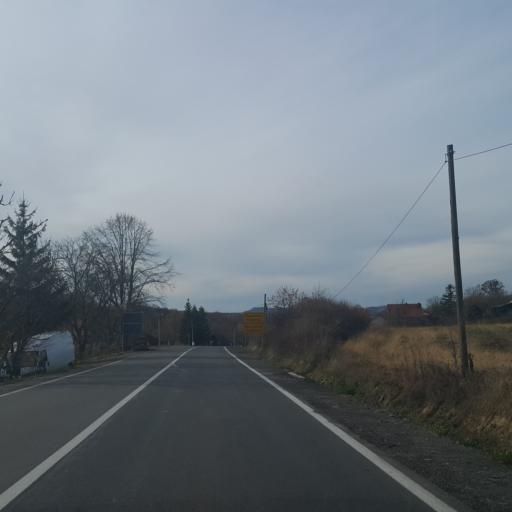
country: RS
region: Central Serbia
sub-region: Sumadijski Okrug
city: Arangelovac
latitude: 44.3421
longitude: 20.4148
